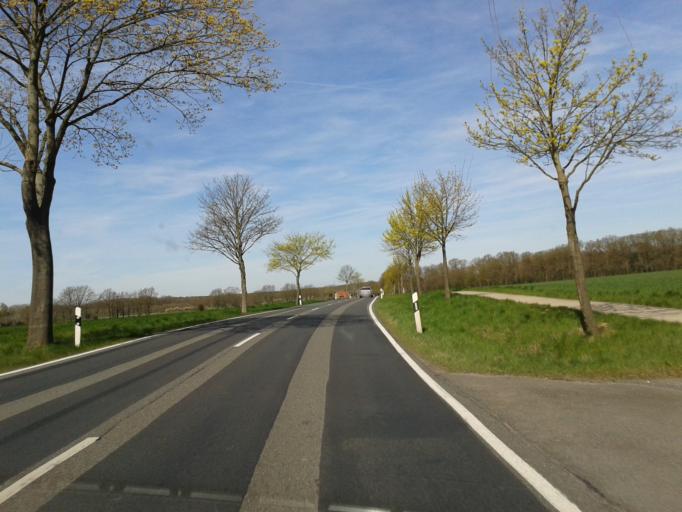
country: DE
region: Lower Saxony
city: Gerdau
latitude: 52.9581
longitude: 10.4271
